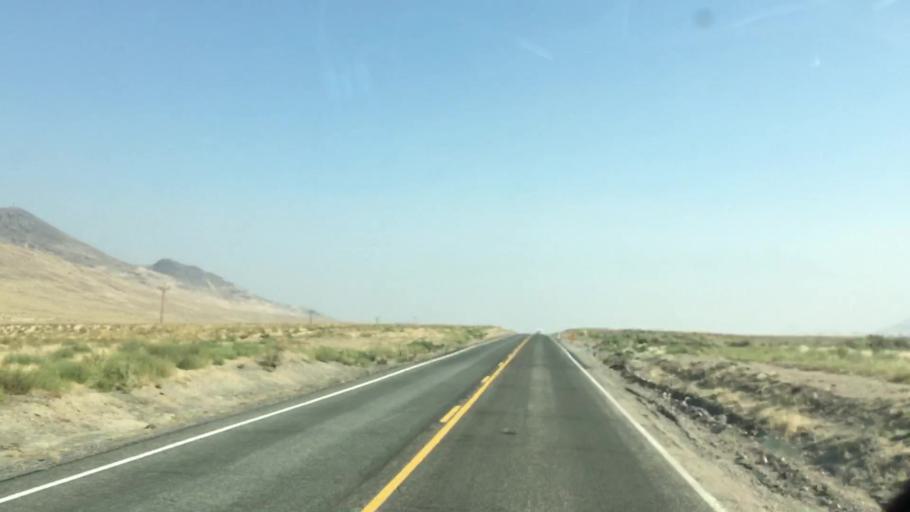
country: US
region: Nevada
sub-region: Lyon County
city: Fernley
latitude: 40.4039
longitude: -119.3337
